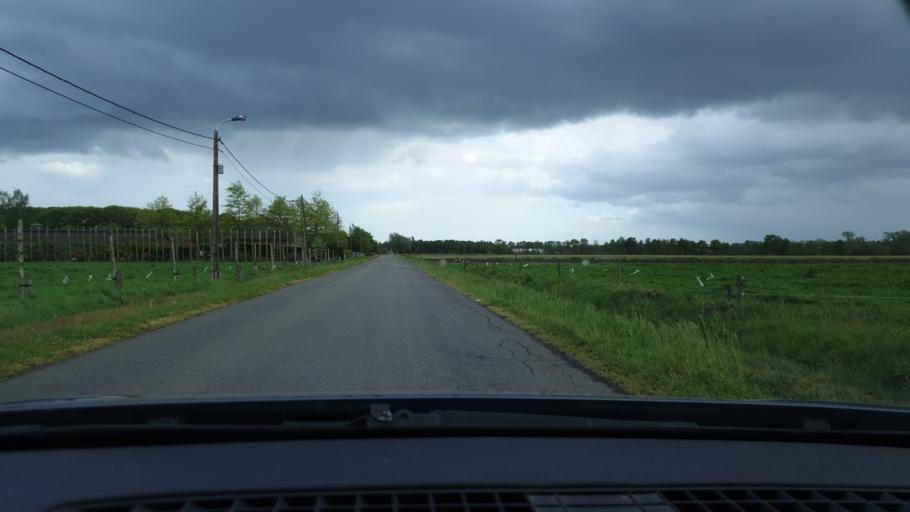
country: BE
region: Flanders
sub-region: Provincie Antwerpen
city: Geel
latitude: 51.1993
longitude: 4.9934
